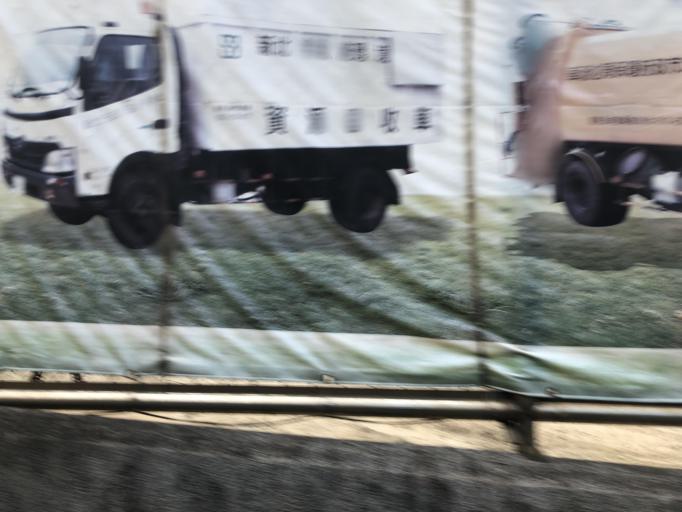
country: TW
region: Taiwan
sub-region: Keelung
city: Keelung
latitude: 25.2283
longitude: 121.6399
